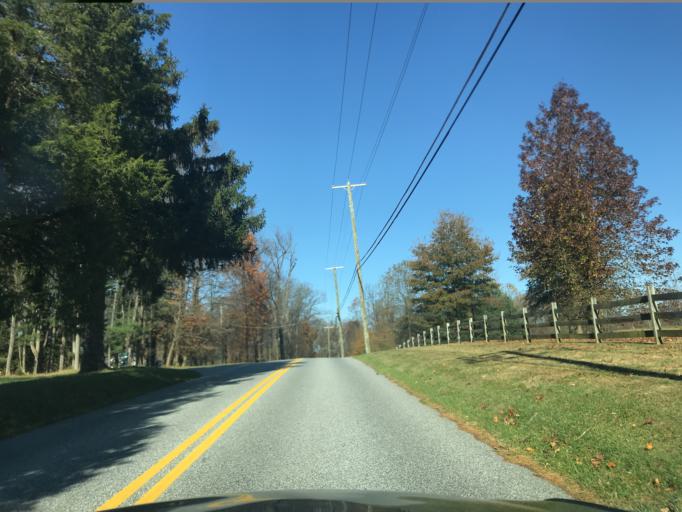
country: US
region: Maryland
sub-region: Baltimore County
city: Hampton
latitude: 39.5023
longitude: -76.5503
